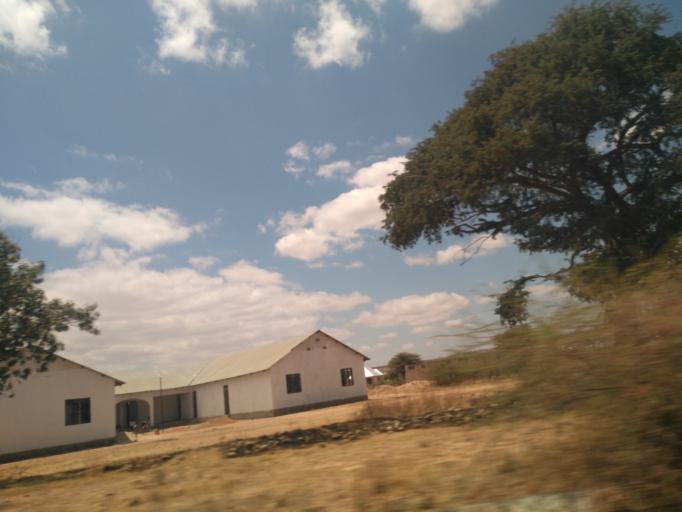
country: TZ
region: Dodoma
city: Kisasa
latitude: -6.1722
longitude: 35.7896
